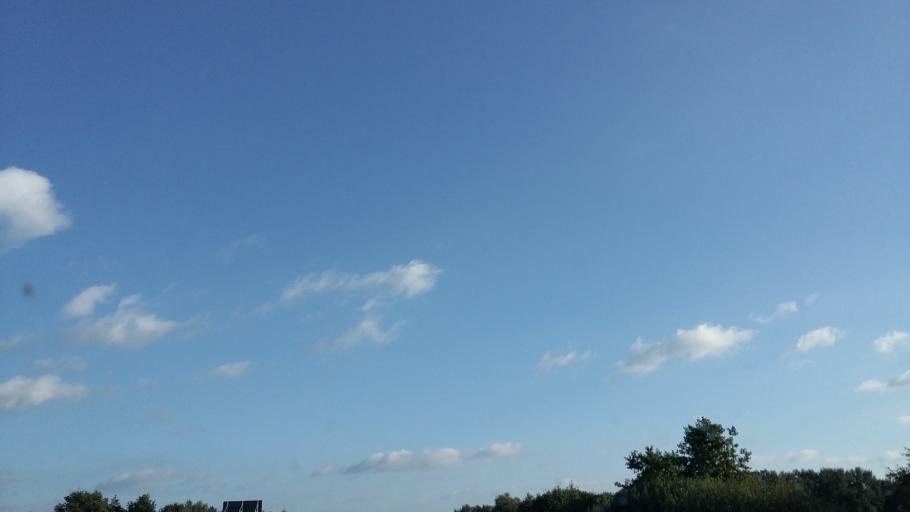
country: DE
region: Lower Saxony
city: Schiffdorf
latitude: 53.5424
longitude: 8.6196
